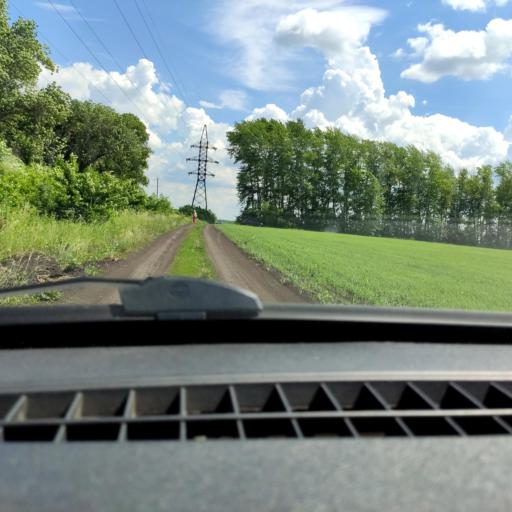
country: RU
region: Bashkortostan
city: Kabakovo
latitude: 54.5187
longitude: 56.0808
